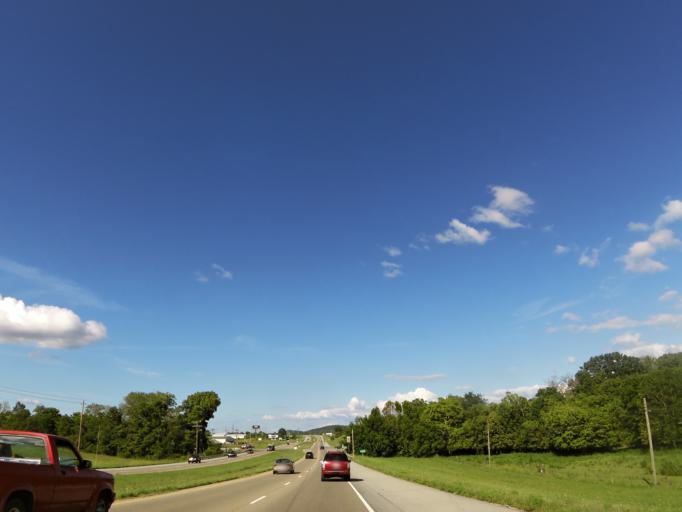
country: US
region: Tennessee
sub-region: Greene County
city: Tusculum
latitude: 36.1864
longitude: -82.7385
